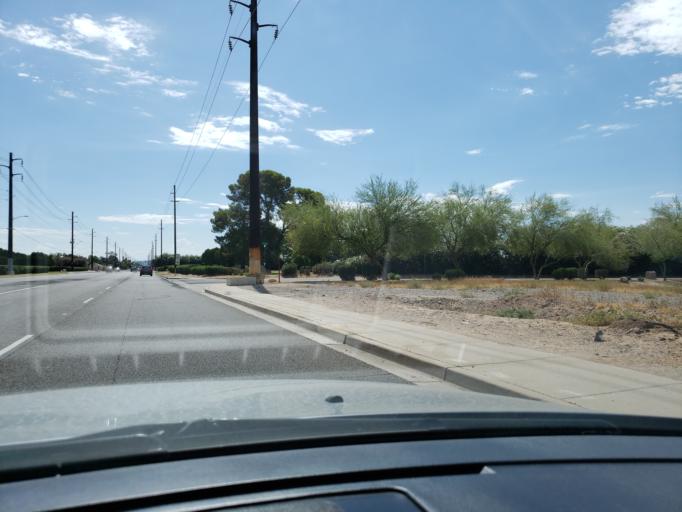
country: US
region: Arizona
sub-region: Maricopa County
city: Glendale
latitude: 33.5529
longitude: -112.1955
